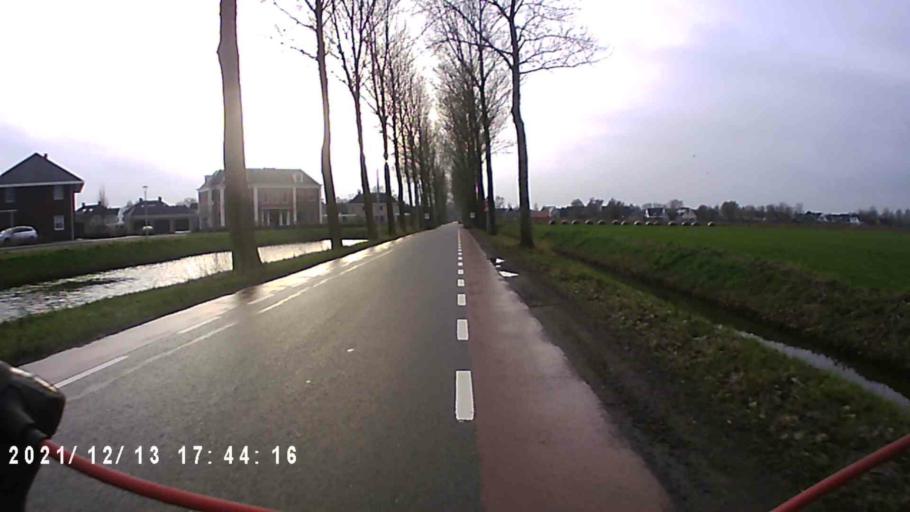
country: NL
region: Groningen
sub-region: Gemeente Bedum
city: Bedum
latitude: 53.2825
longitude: 6.7013
